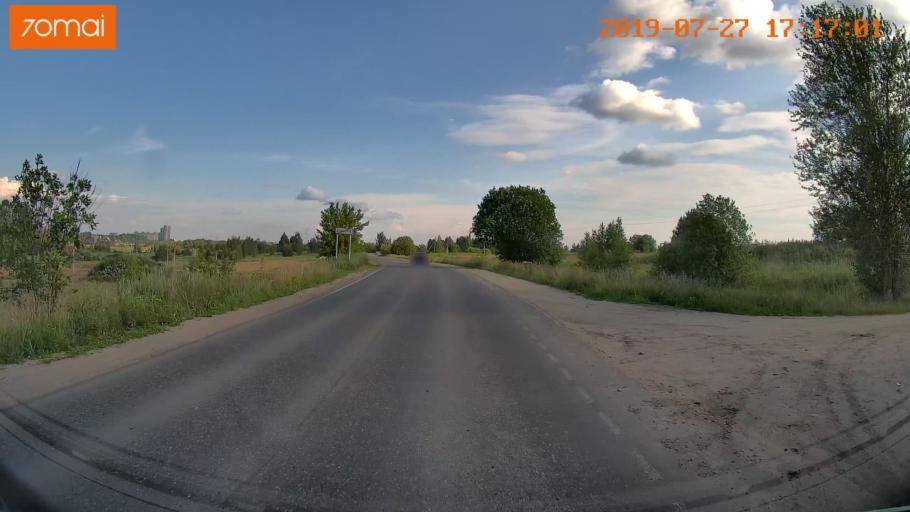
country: RU
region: Ivanovo
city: Novo-Talitsy
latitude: 57.0412
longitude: 40.8911
